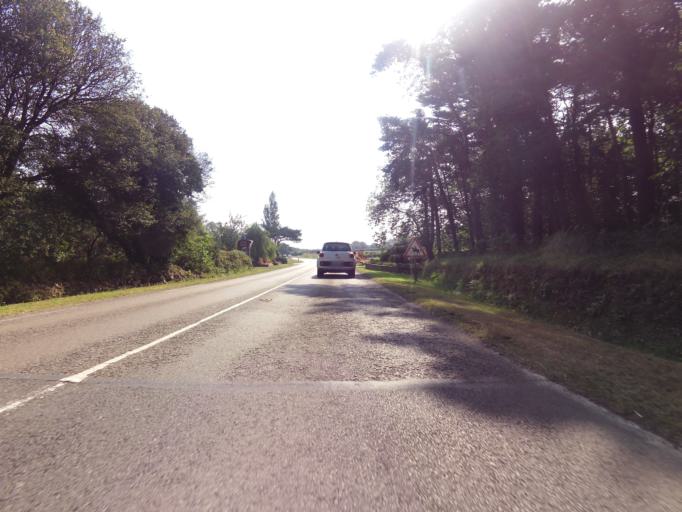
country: FR
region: Brittany
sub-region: Departement du Finistere
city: Plouhinec
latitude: 48.0123
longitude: -4.4735
